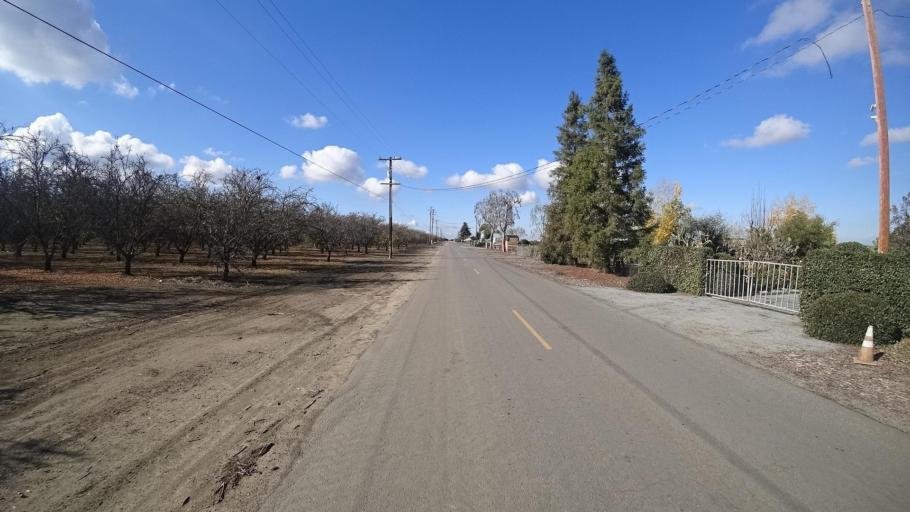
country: US
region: California
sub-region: Kern County
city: McFarland
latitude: 35.6599
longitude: -119.2463
